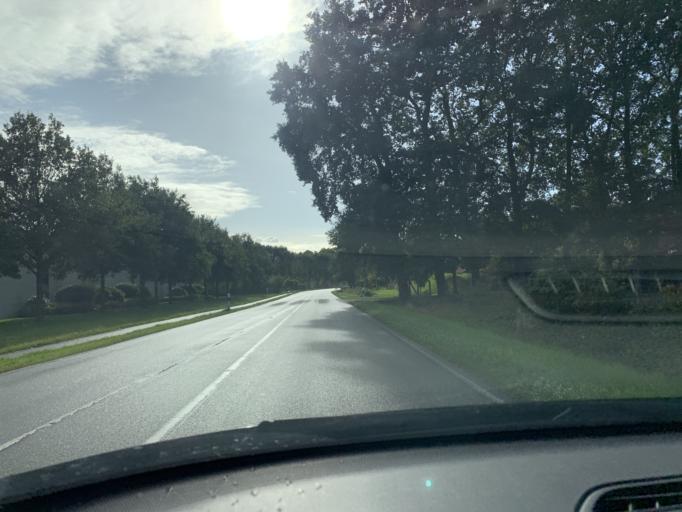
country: DE
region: Lower Saxony
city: Bad Zwischenahn
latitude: 53.1881
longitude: 7.9672
